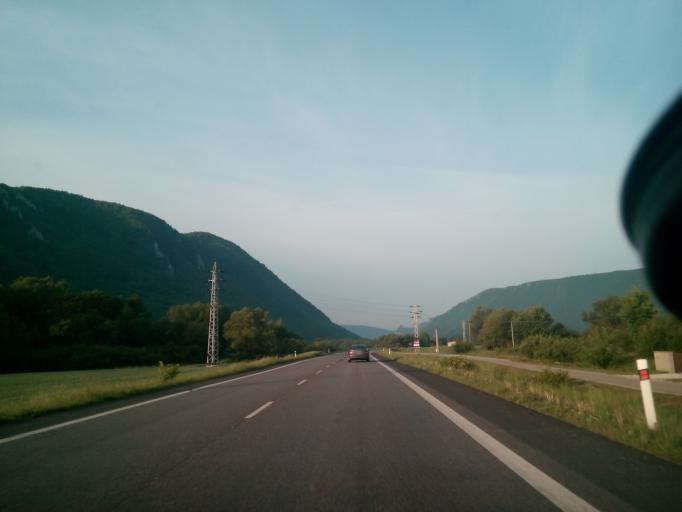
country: SK
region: Kosicky
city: Roznava
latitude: 48.6290
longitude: 20.5031
